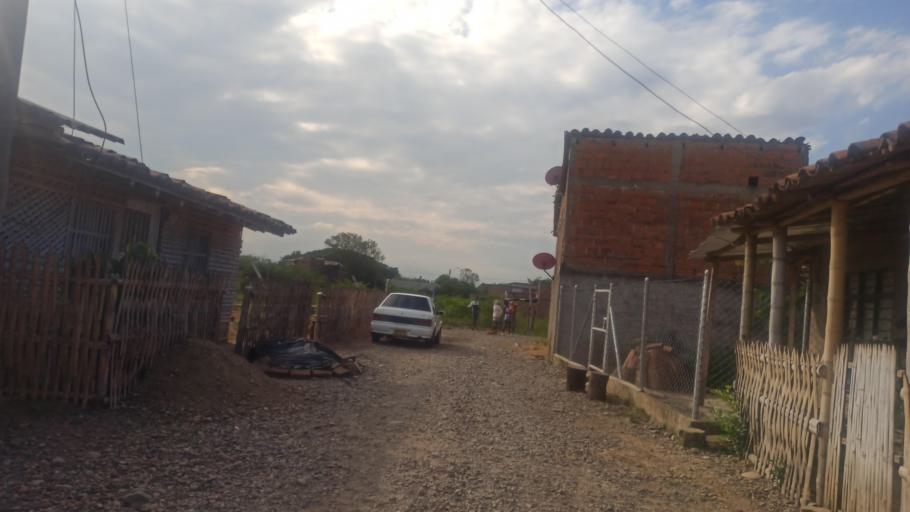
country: CO
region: Valle del Cauca
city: Jamundi
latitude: 3.1302
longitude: -76.5577
